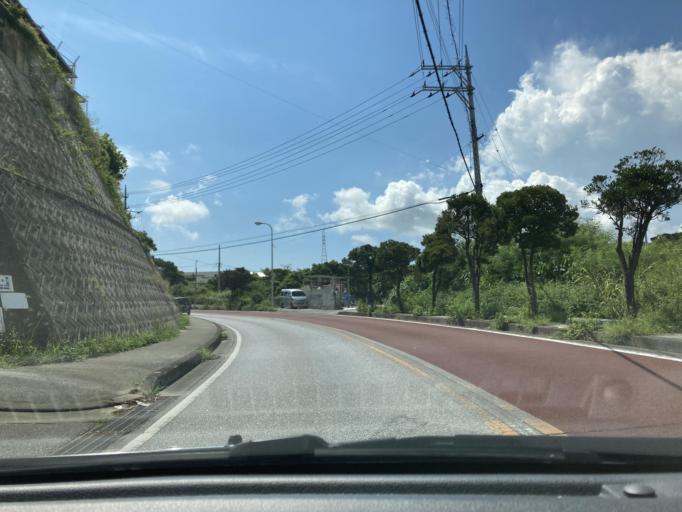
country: JP
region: Okinawa
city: Tomigusuku
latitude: 26.1717
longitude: 127.7527
